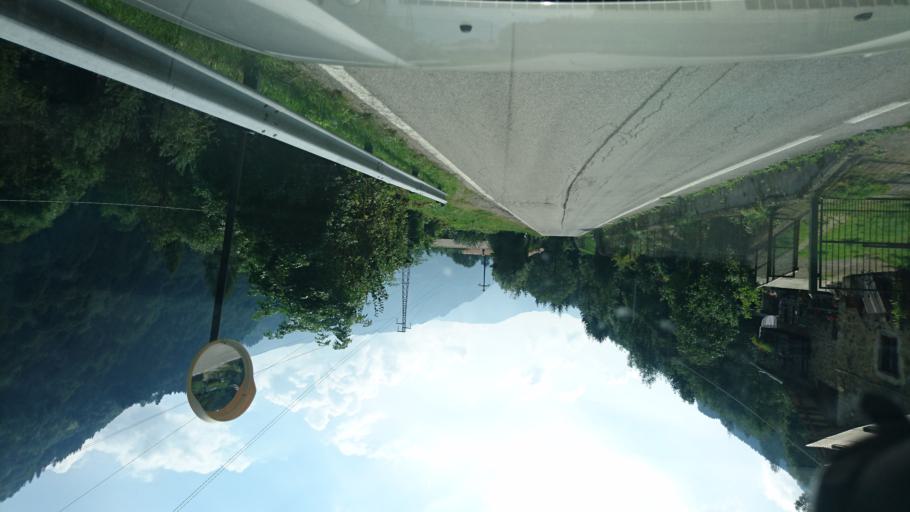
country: IT
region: Lombardy
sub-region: Provincia di Brescia
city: Bagolino
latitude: 45.8606
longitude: 10.4547
